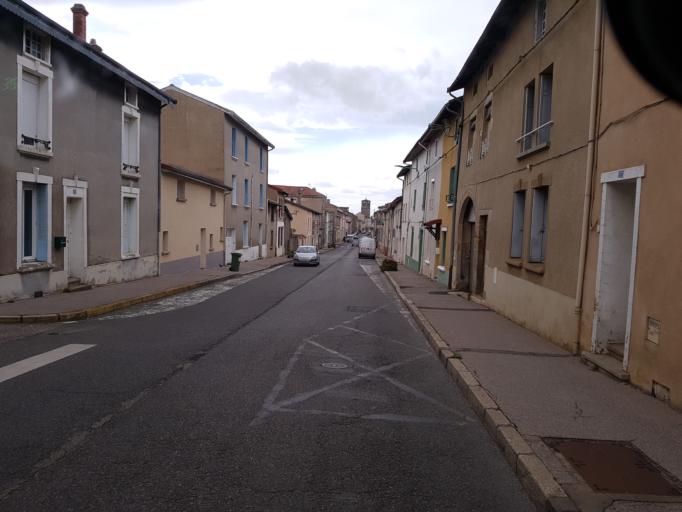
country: FR
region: Rhone-Alpes
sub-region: Departement de la Loire
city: Chazelles-sur-Lyon
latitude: 45.6413
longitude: 4.3954
